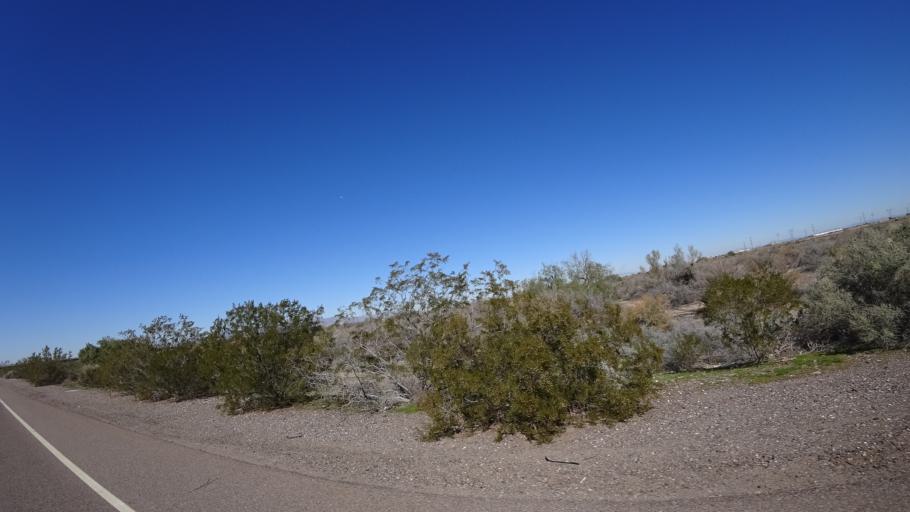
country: US
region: Arizona
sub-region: Maricopa County
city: Goodyear
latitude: 33.3878
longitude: -112.3875
